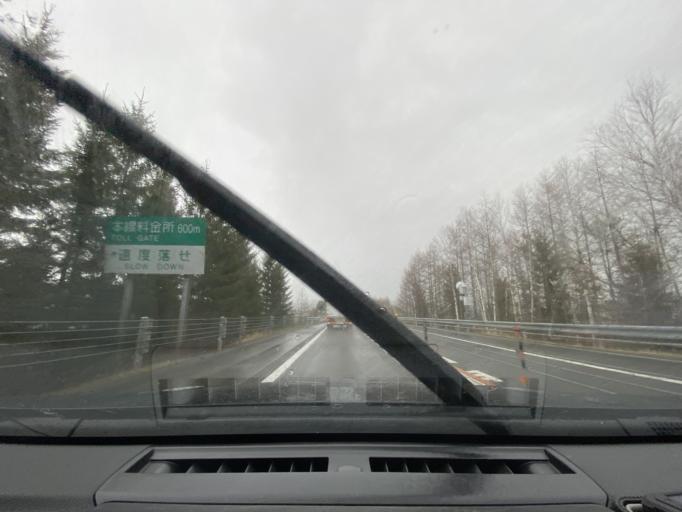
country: JP
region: Hokkaido
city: Otofuke
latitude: 42.9949
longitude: 143.4297
